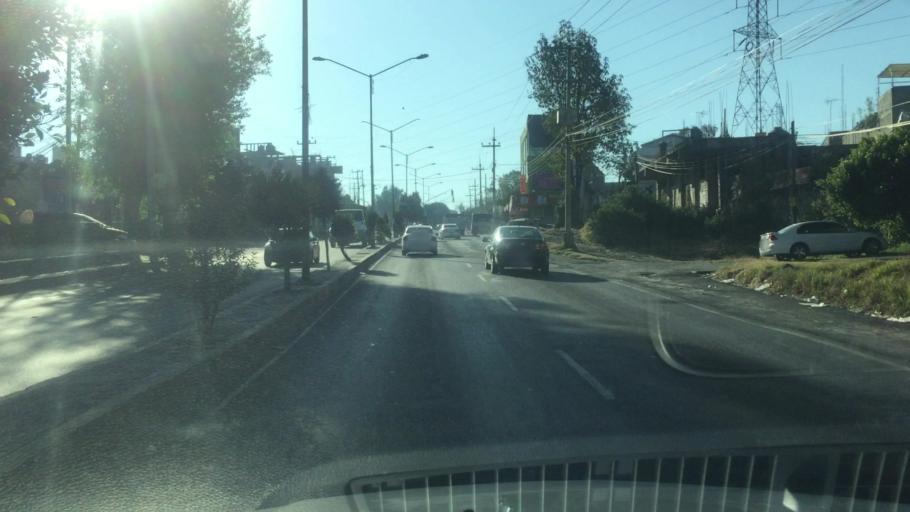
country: MX
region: Mexico City
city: Tlalpan
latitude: 19.2752
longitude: -99.2079
